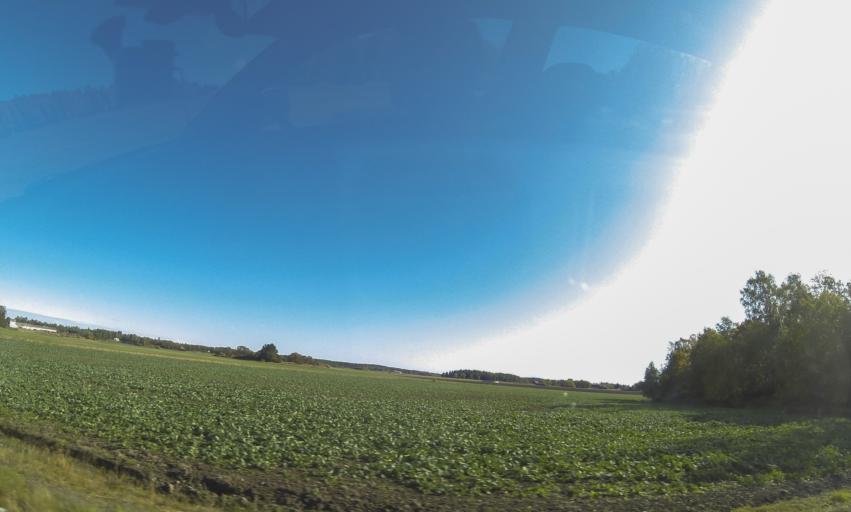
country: SE
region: Soedermanland
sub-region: Eskilstuna Kommun
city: Kvicksund
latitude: 59.5604
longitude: 16.4084
